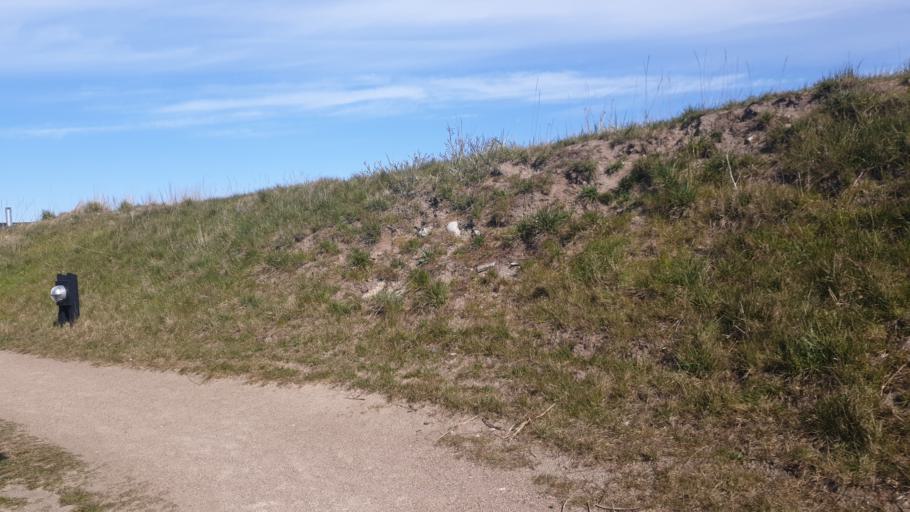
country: DK
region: North Denmark
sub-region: Hjorring Kommune
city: Hjorring
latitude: 57.4962
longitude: 9.8382
